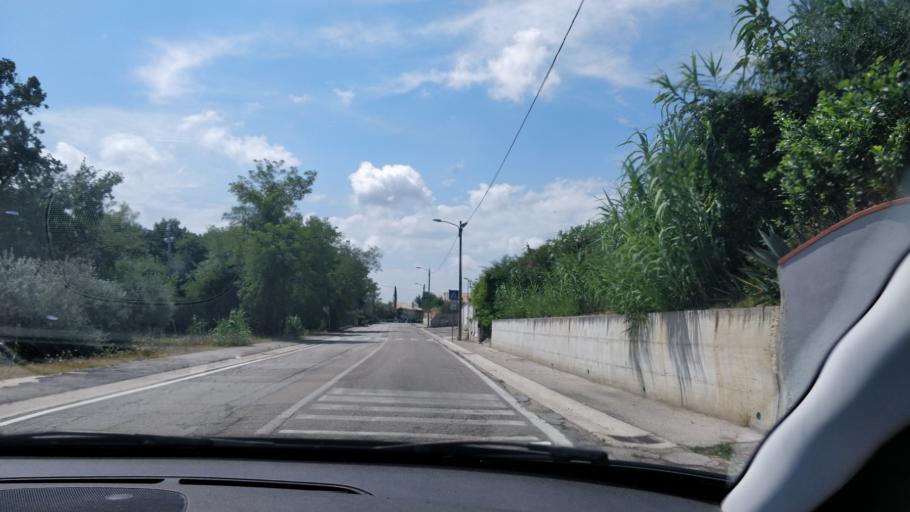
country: IT
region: Abruzzo
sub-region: Provincia di Chieti
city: Francavilla al Mare
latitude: 42.4237
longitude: 14.2668
